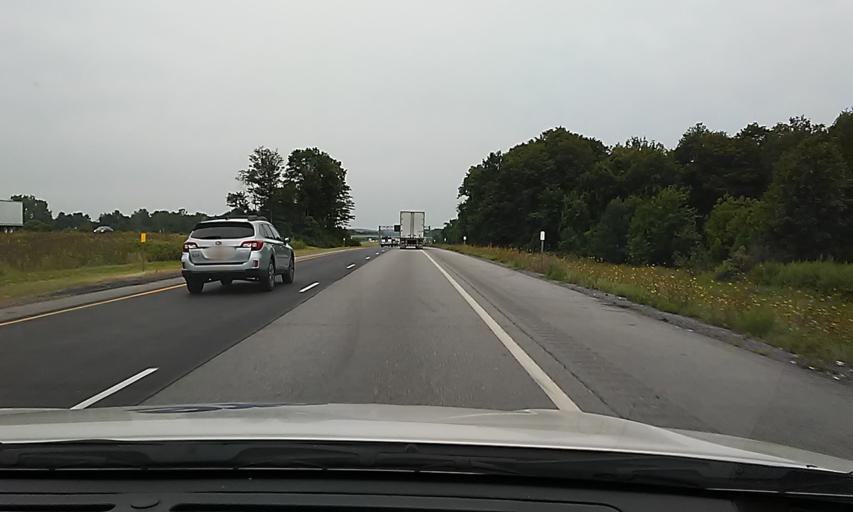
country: US
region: New York
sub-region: Genesee County
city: Le Roy
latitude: 43.0259
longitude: -78.0564
